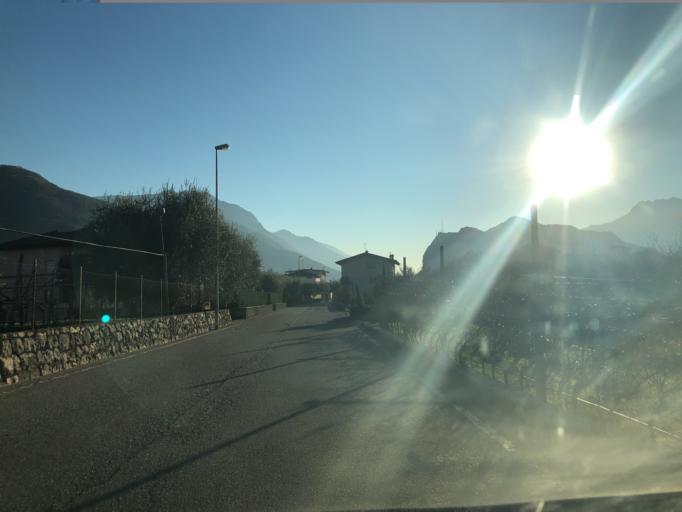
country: IT
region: Trentino-Alto Adige
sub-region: Provincia di Trento
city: Arco
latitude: 45.9087
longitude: 10.8898
